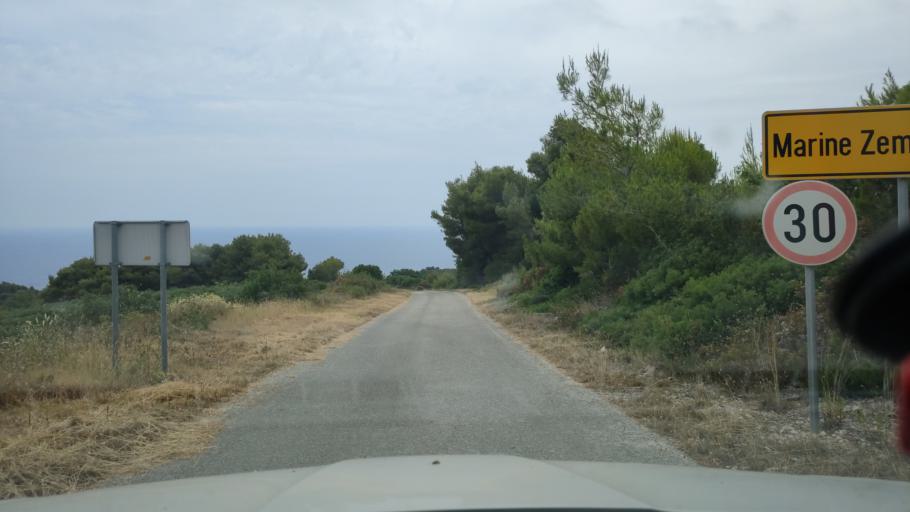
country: HR
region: Splitsko-Dalmatinska
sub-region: Grad Vis
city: Vis
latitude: 43.0263
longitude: 16.1682
